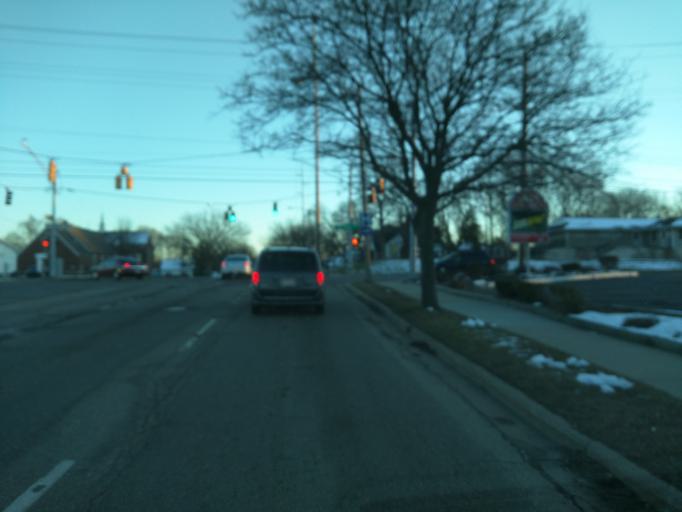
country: US
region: Michigan
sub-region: Ingham County
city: Lansing
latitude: 42.7123
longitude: -84.5382
